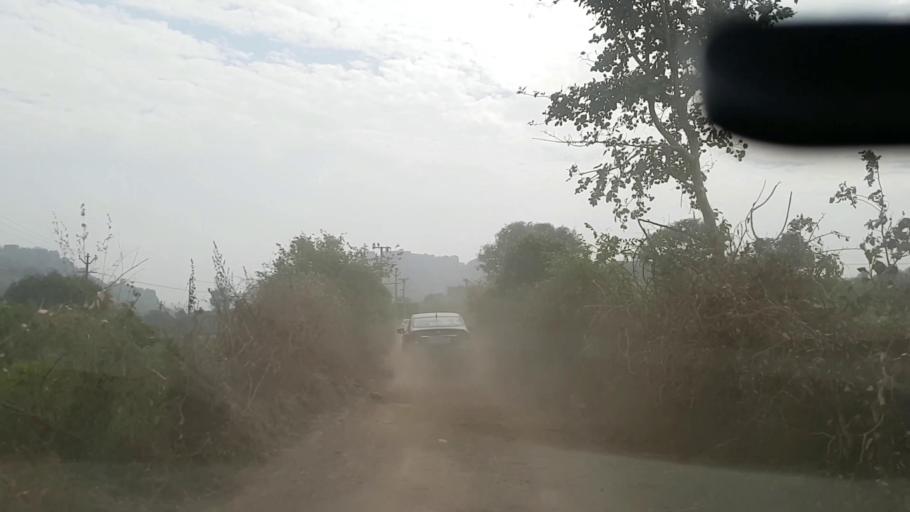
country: IN
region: Telangana
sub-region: Rangareddi
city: Lal Bahadur Nagar
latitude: 17.1813
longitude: 78.7898
